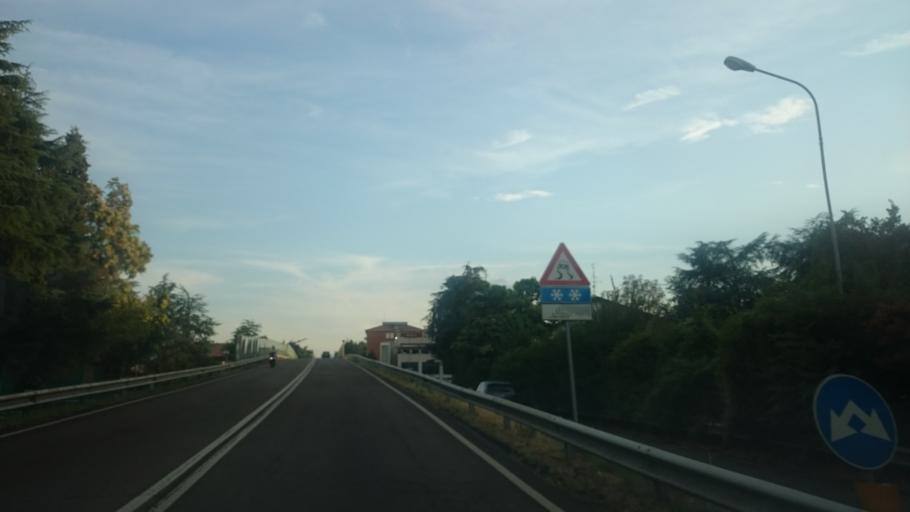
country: IT
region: Emilia-Romagna
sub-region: Provincia di Reggio Emilia
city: Reggio nell'Emilia
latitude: 44.6799
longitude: 10.6421
